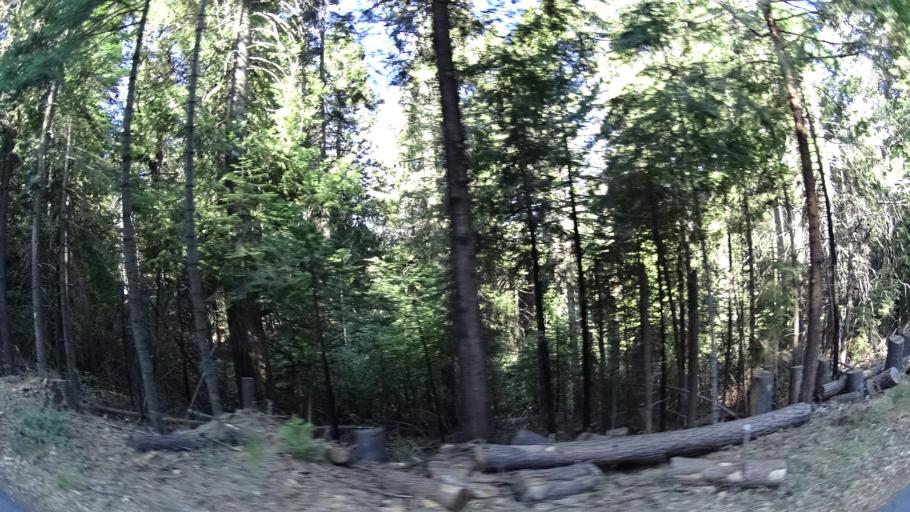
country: US
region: California
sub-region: Calaveras County
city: Arnold
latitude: 38.2629
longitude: -120.3173
